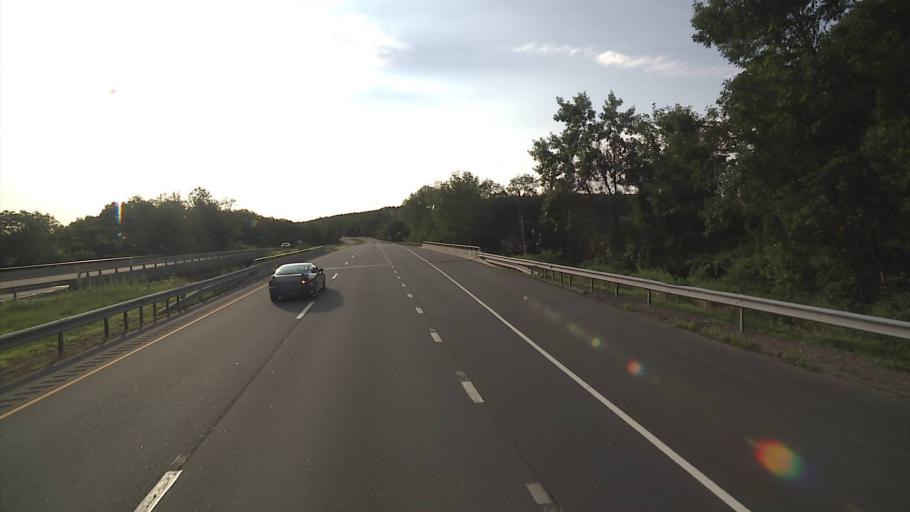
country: US
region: Connecticut
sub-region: New London County
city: Montville Center
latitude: 41.5622
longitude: -72.1656
